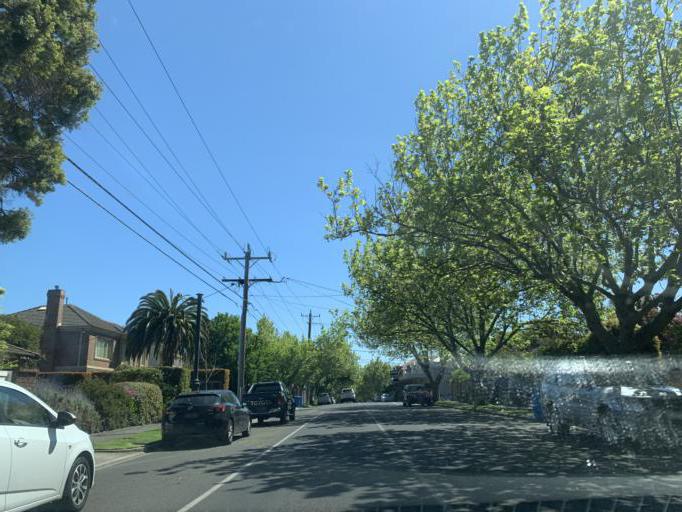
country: AU
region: Victoria
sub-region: Bayside
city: Hampton
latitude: -37.9259
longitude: 145.0015
